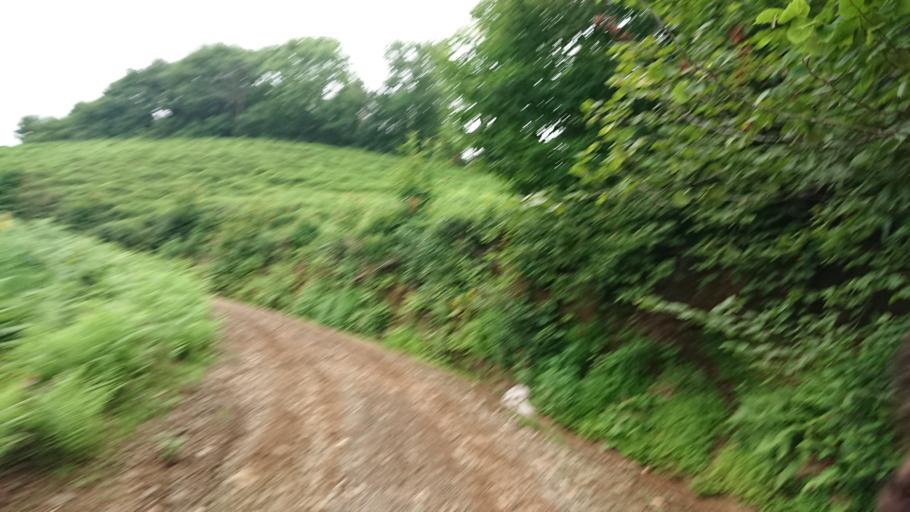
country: TR
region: Rize
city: Rize
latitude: 40.9895
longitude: 40.5073
